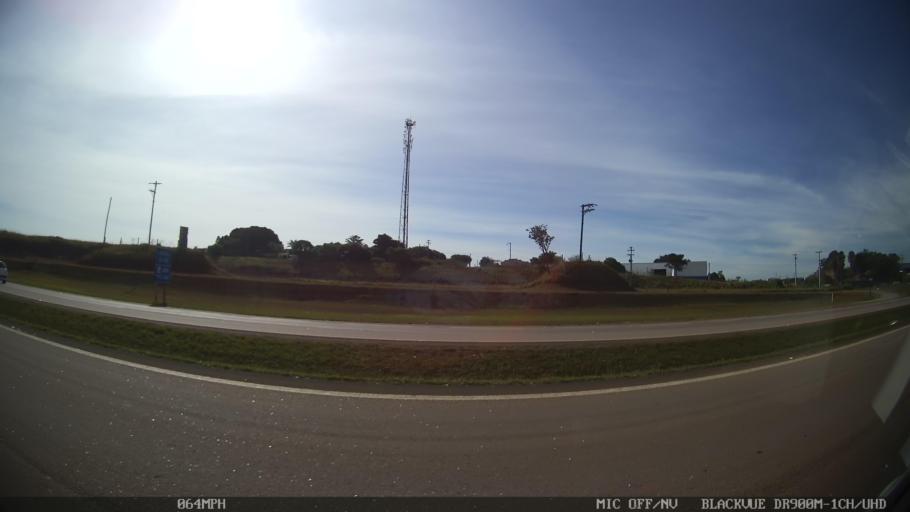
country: BR
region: Sao Paulo
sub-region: Rio Das Pedras
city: Rio das Pedras
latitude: -22.7853
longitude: -47.5858
